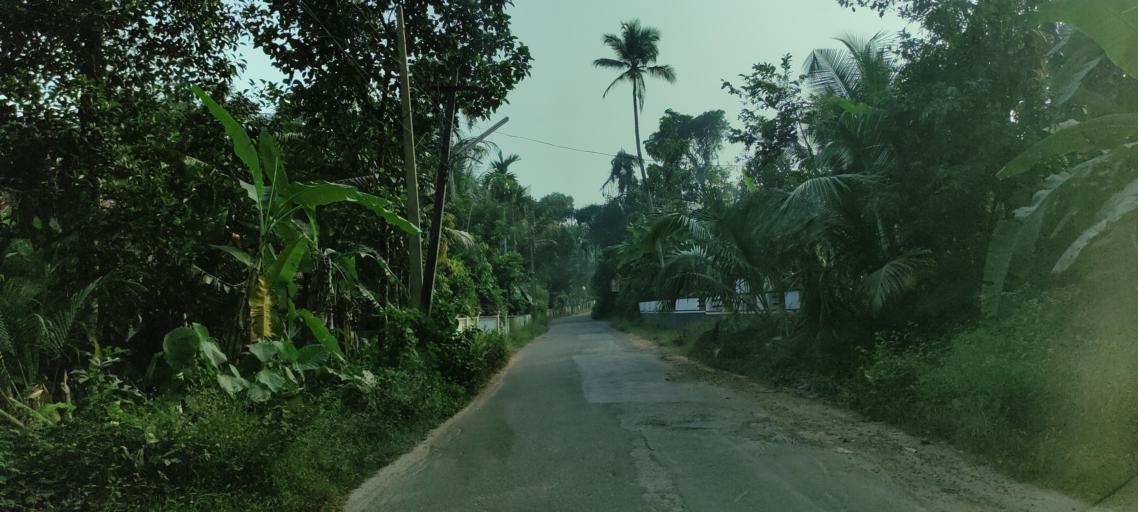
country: IN
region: Kerala
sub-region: Ernakulam
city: Piravam
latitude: 9.7801
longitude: 76.4981
